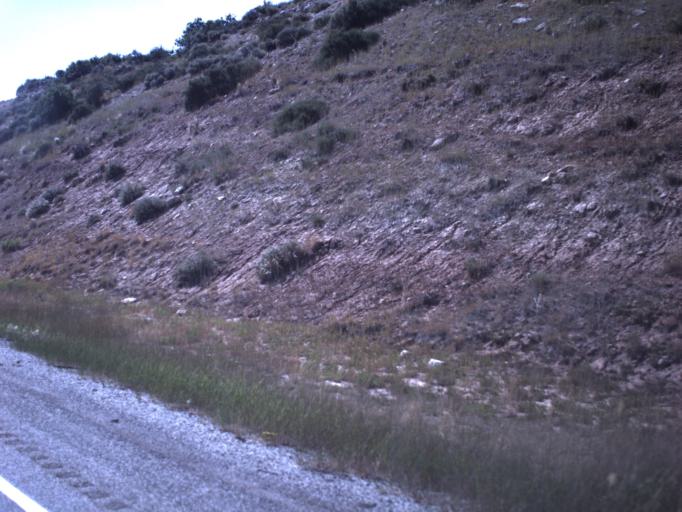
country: US
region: Utah
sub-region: Summit County
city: Francis
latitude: 40.2028
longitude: -110.9836
